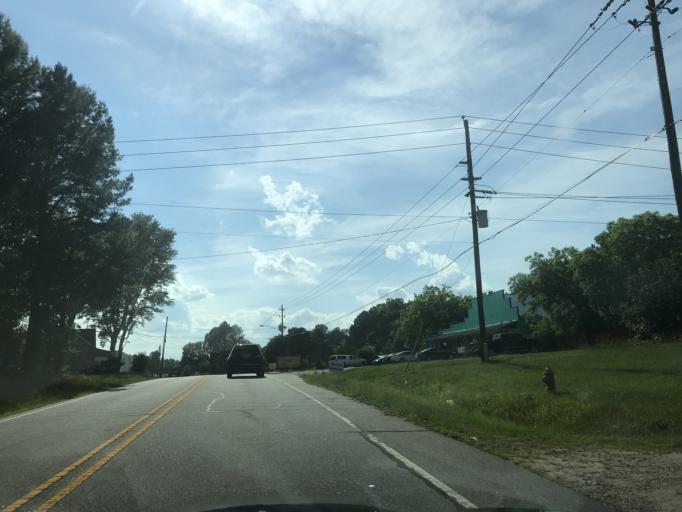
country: US
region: North Carolina
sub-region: Nash County
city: Spring Hope
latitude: 35.9518
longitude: -78.0990
